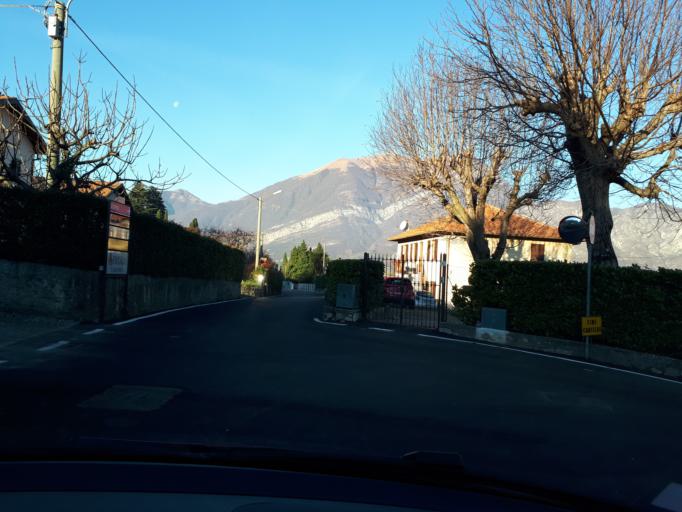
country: IT
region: Lombardy
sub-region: Provincia di Como
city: Bellagio
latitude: 45.9762
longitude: 9.2573
